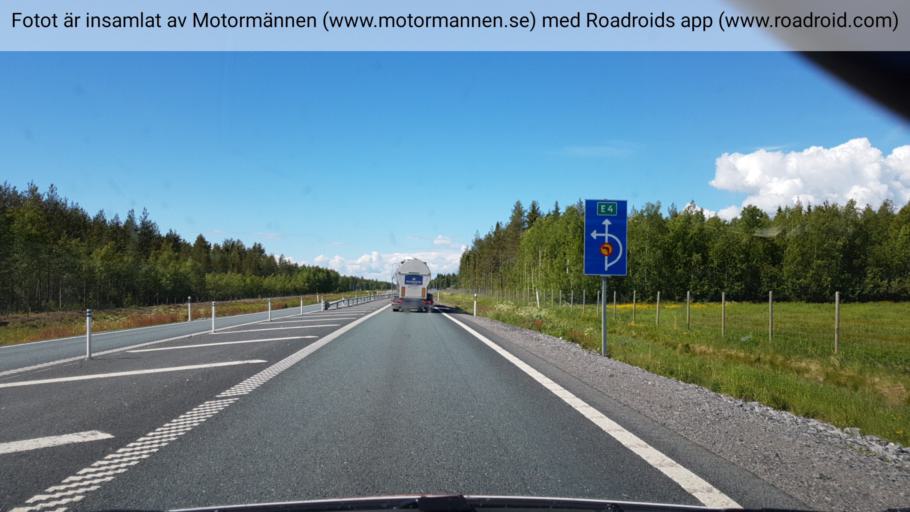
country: SE
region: Norrbotten
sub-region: Kalix Kommun
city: Kalix
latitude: 65.8277
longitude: 23.2330
